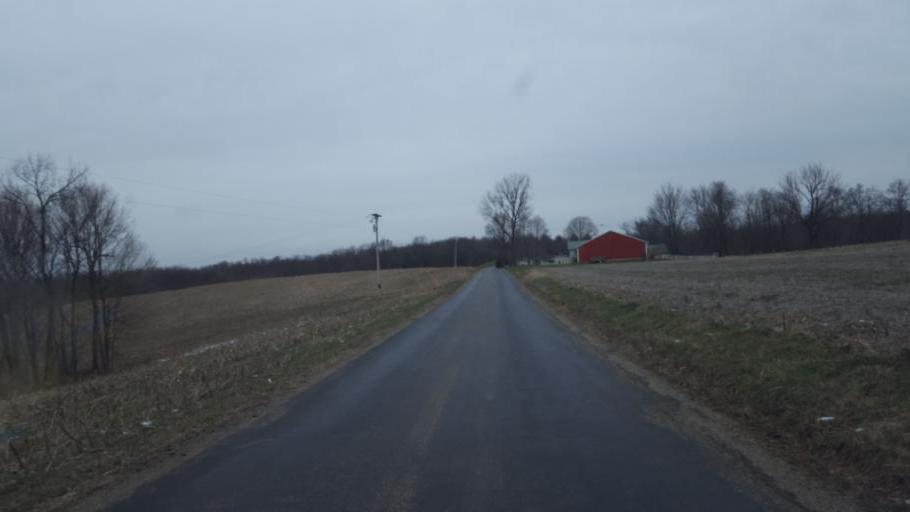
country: US
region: Ohio
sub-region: Sandusky County
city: Bellville
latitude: 40.5695
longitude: -82.4249
